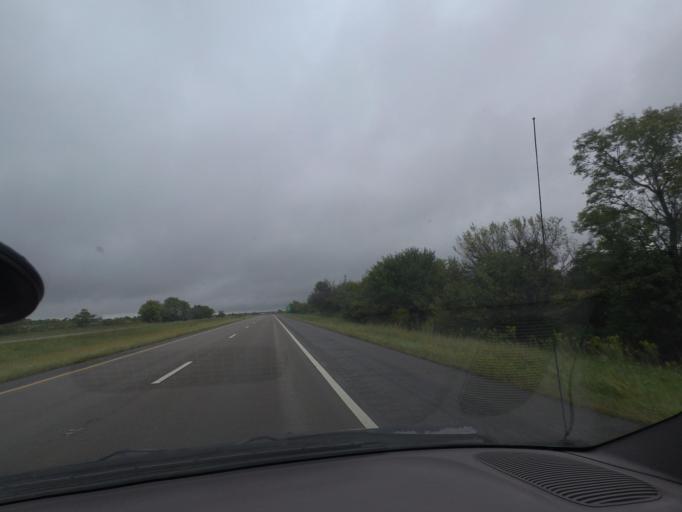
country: US
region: Illinois
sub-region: Piatt County
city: Monticello
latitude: 40.0998
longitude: -88.4954
